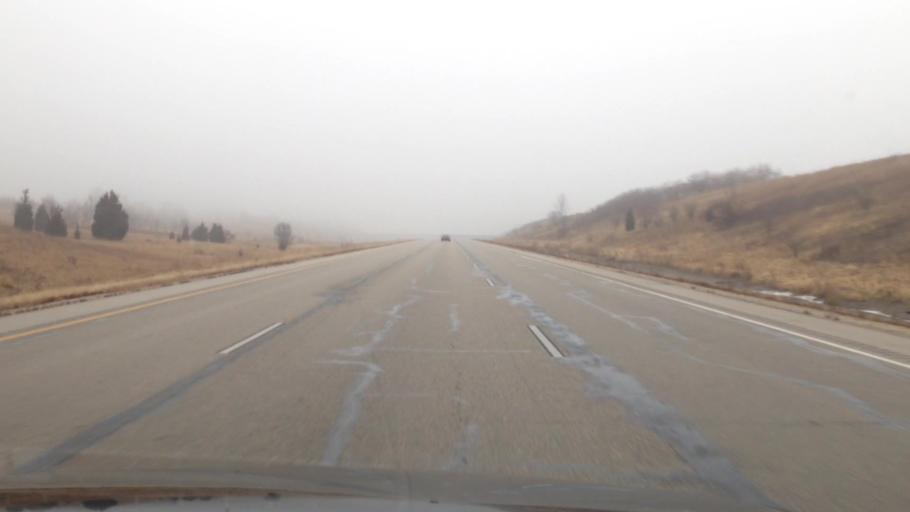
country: US
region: Wisconsin
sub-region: Walworth County
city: East Troy
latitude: 42.7365
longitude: -88.4553
